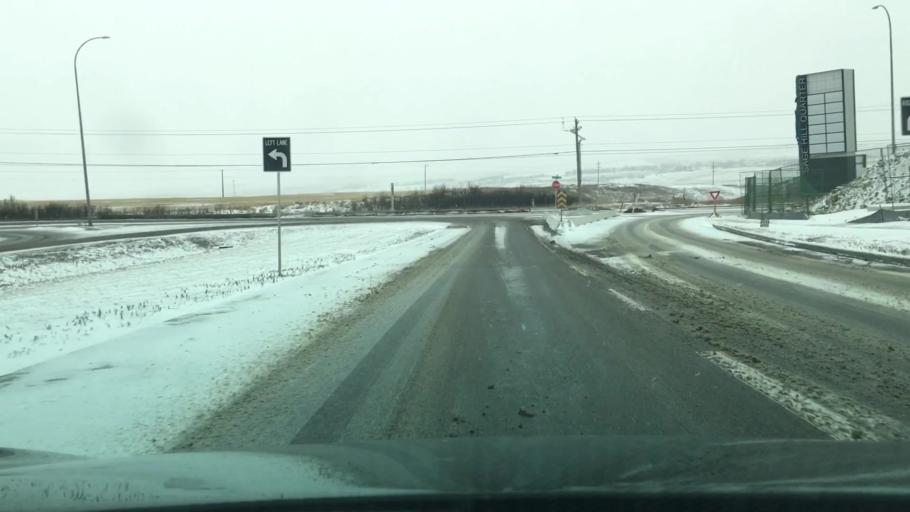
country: CA
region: Alberta
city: Calgary
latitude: 51.1824
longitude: -114.1610
